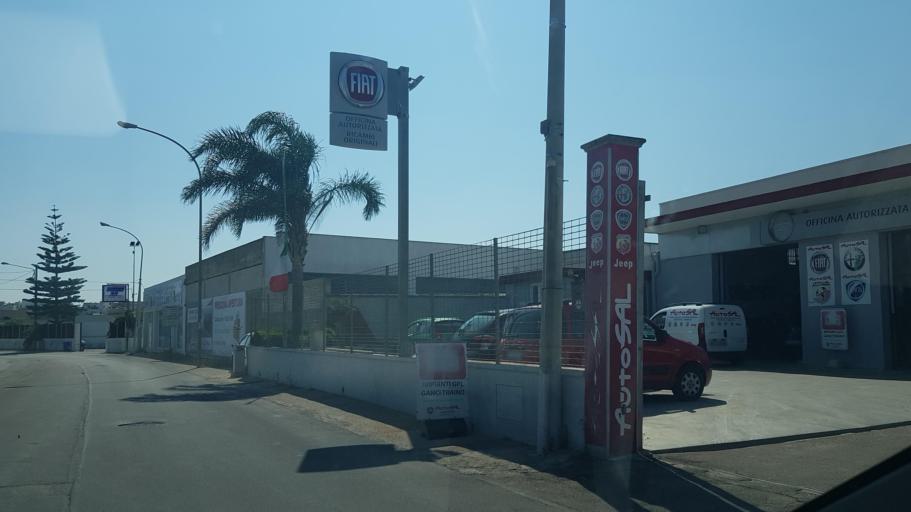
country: IT
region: Apulia
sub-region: Provincia di Lecce
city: Ugento
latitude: 39.9345
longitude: 18.1672
